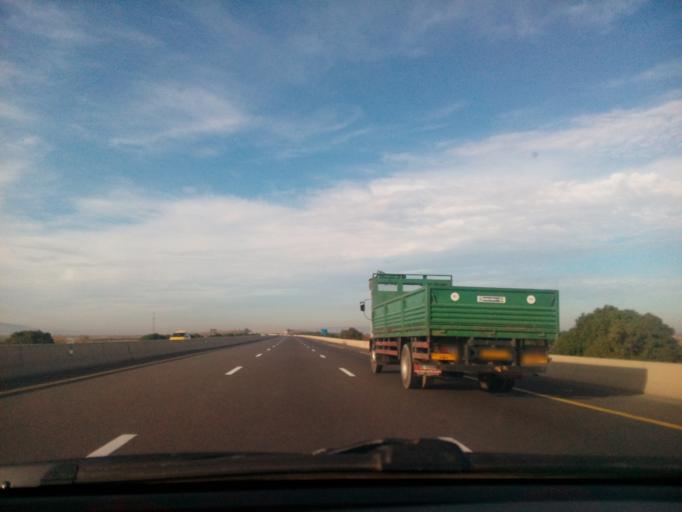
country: DZ
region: Mascara
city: Sig
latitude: 35.5876
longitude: -0.1075
